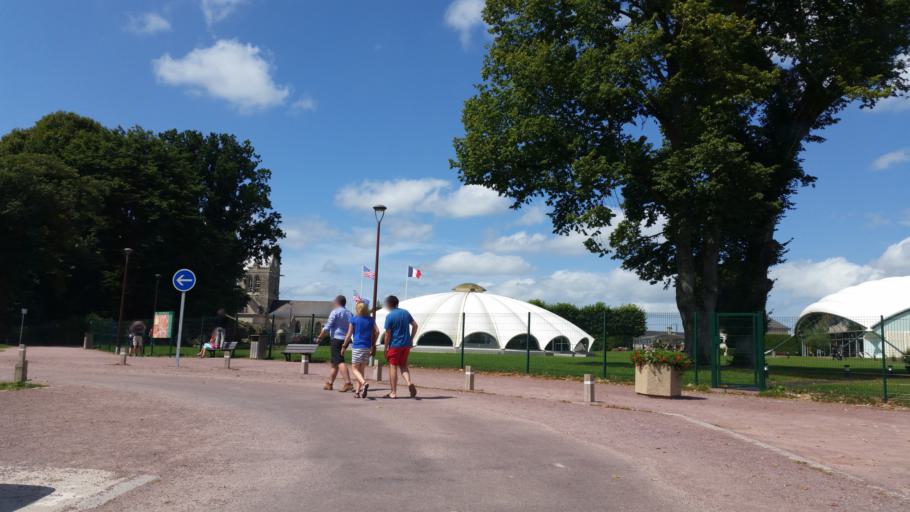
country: FR
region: Lower Normandy
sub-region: Departement de la Manche
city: Sainte-Mere-Eglise
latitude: 49.4075
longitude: -1.3144
